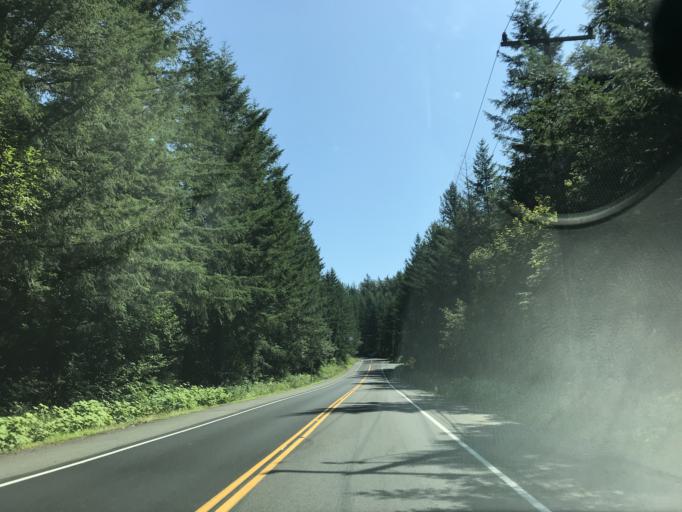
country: US
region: Washington
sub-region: King County
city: Ravensdale
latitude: 47.3565
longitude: -121.8871
